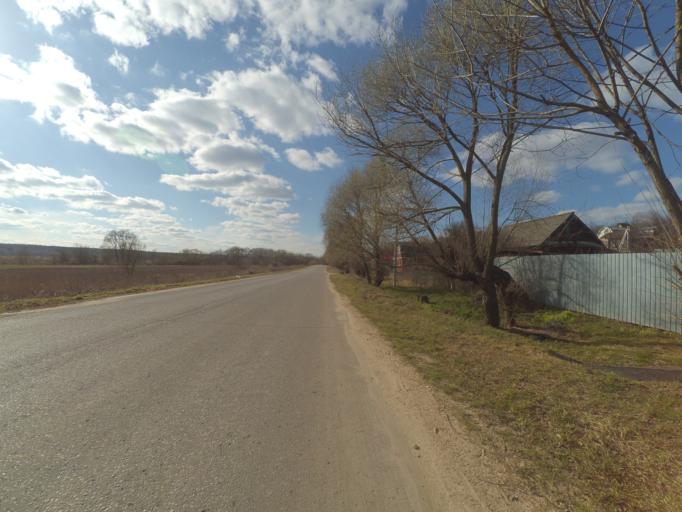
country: RU
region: Moskovskaya
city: Bol'shoye Gryzlovo
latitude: 54.8735
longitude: 37.8271
